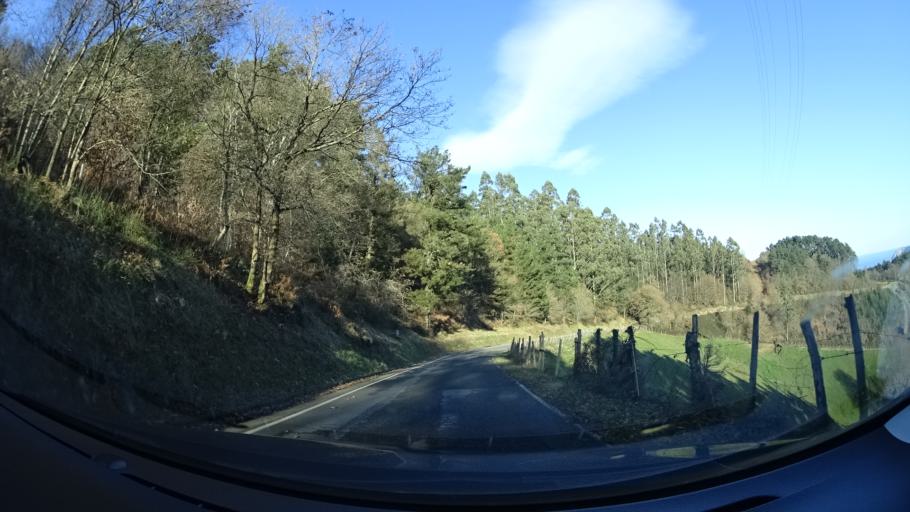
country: ES
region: Basque Country
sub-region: Bizkaia
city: Bermeo
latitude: 43.3996
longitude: -2.7551
